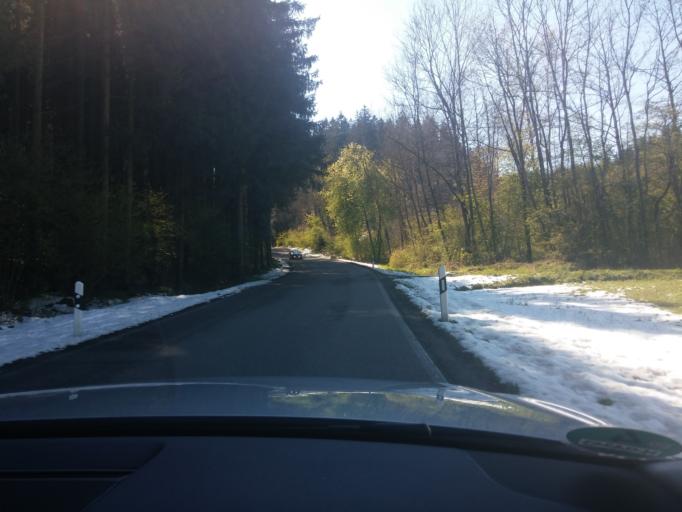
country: DE
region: Baden-Wuerttemberg
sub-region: Tuebingen Region
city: Tannheim
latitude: 47.9726
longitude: 10.0757
